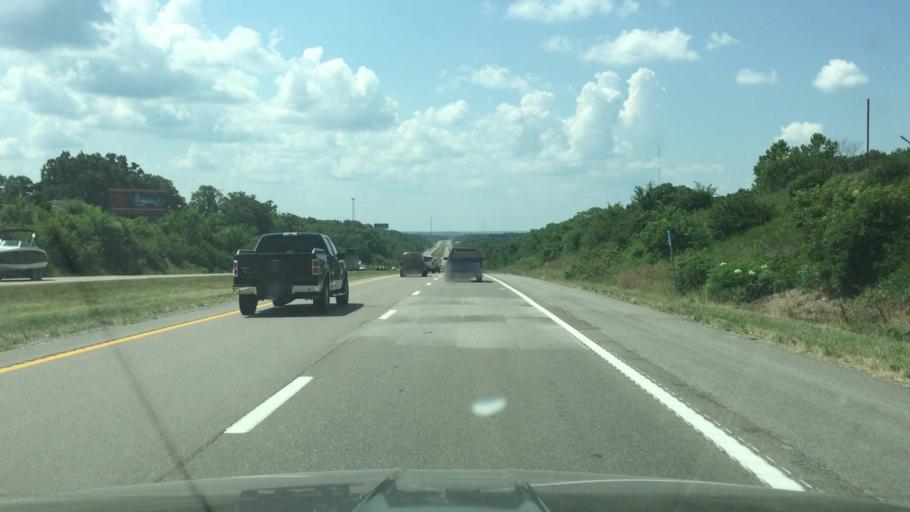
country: US
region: Missouri
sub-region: Miller County
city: Eldon
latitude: 38.2928
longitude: -92.5806
